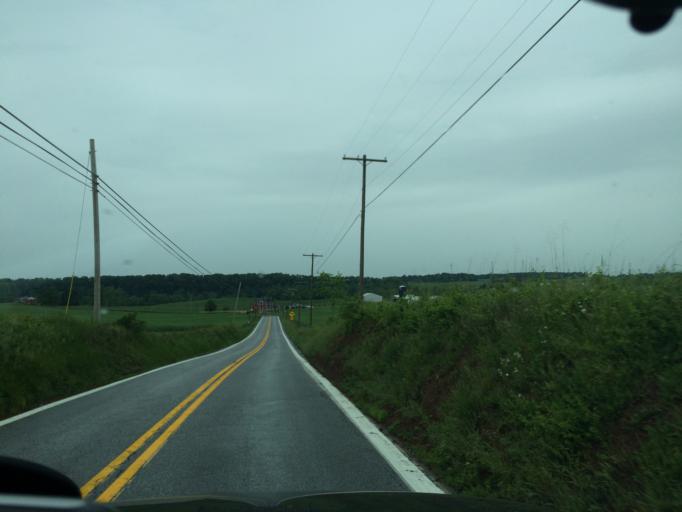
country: US
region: Maryland
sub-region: Carroll County
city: Taneytown
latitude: 39.6056
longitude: -77.2493
